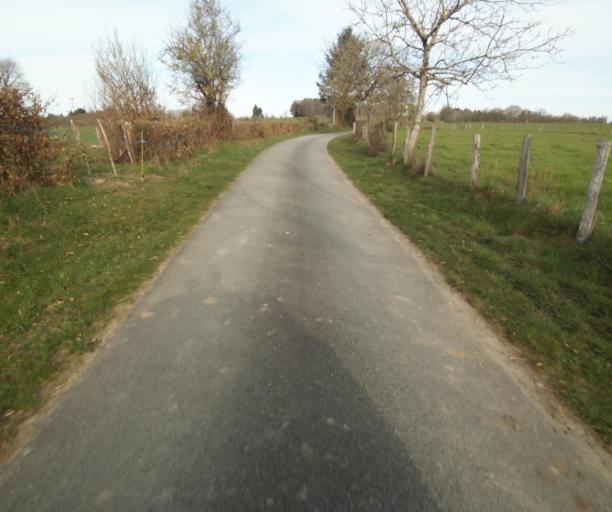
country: FR
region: Limousin
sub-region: Departement de la Correze
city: Chamboulive
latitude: 45.4353
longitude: 1.7921
